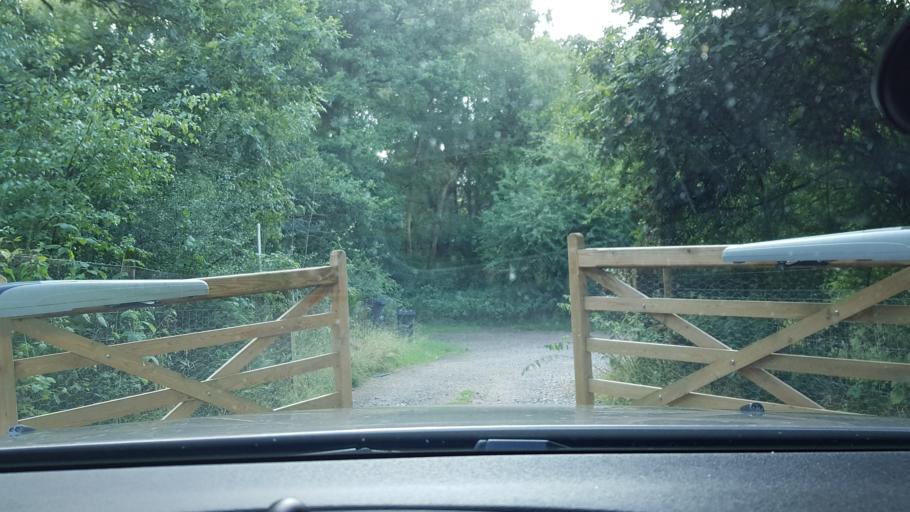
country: GB
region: England
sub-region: Wiltshire
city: Mildenhall
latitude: 51.4040
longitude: -1.6917
